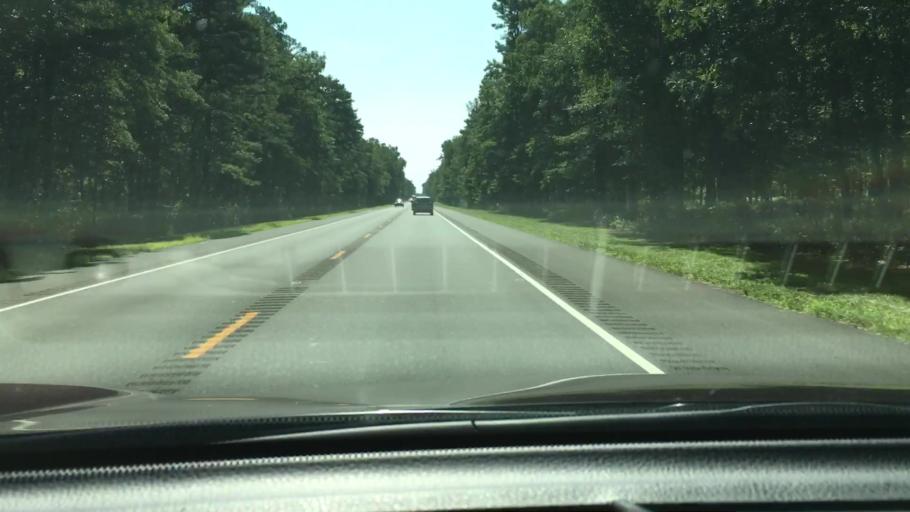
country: US
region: New Jersey
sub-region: Cape May County
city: Woodbine
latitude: 39.3405
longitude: -74.8925
